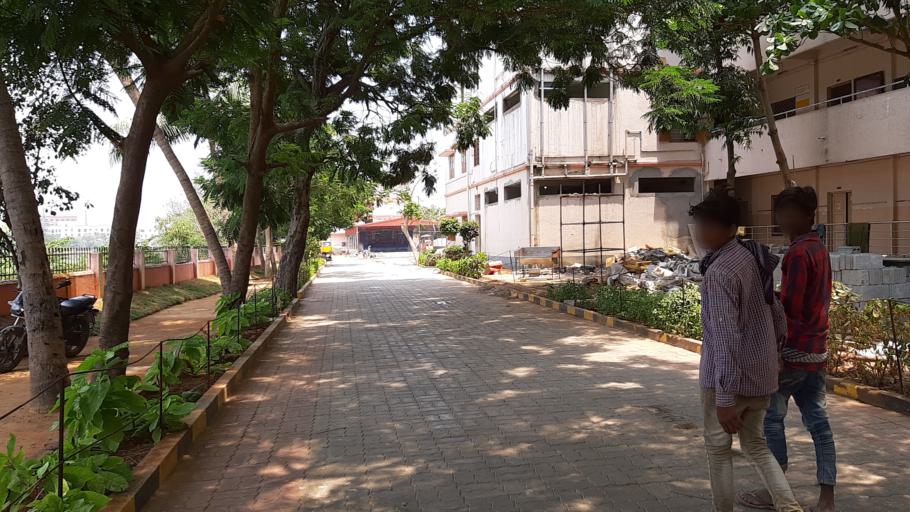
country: IN
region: Tamil Nadu
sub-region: Kancheepuram
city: Saint Thomas Mount
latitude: 13.0249
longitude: 80.1902
